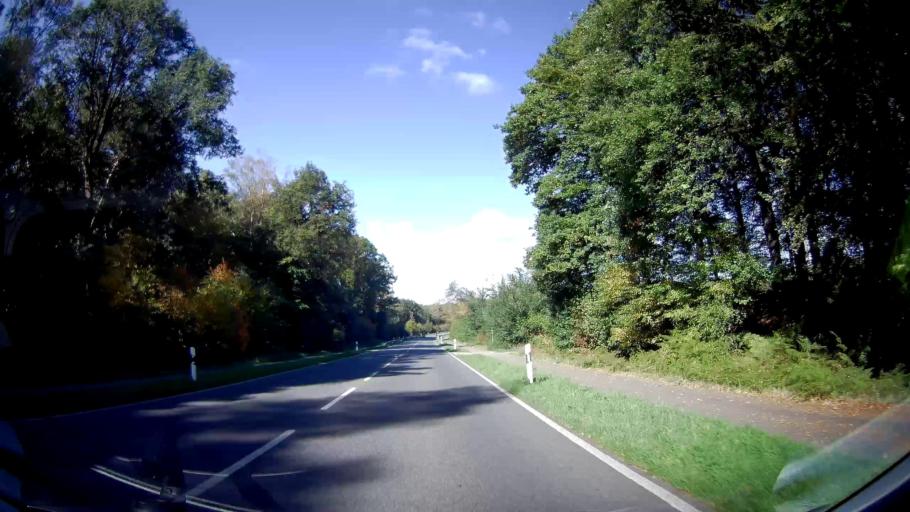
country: DE
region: North Rhine-Westphalia
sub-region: Regierungsbezirk Dusseldorf
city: Hunxe
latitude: 51.6167
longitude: 6.7575
